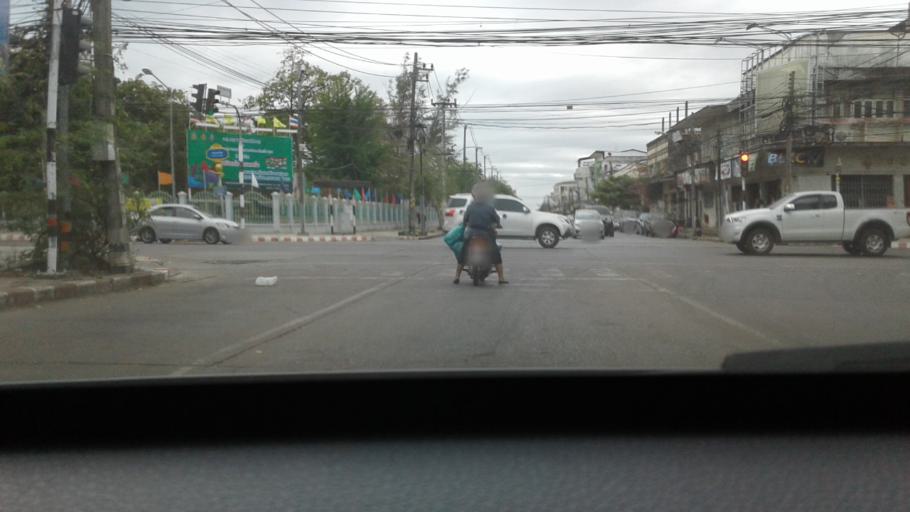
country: TH
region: Changwat Udon Thani
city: Udon Thani
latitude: 17.4033
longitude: 102.7906
